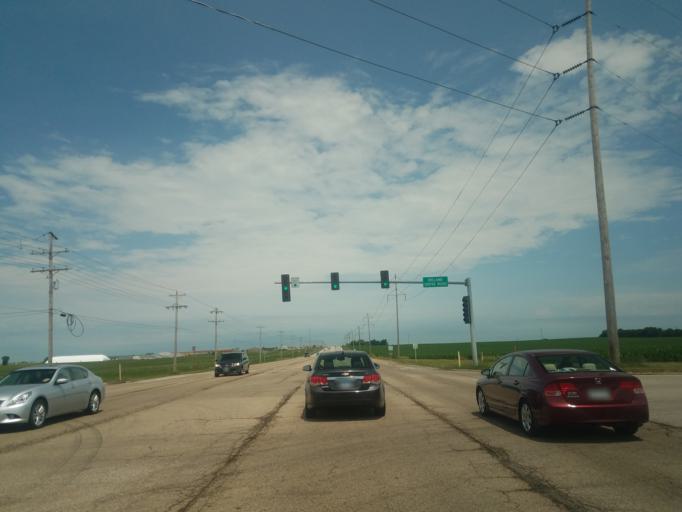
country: US
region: Illinois
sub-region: McLean County
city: Downs
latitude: 40.4583
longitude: -88.9018
